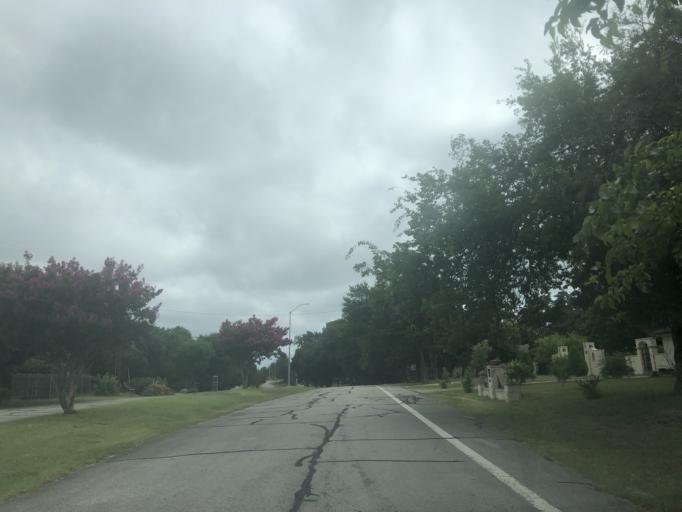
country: US
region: Texas
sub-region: Dallas County
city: Duncanville
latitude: 32.6721
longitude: -96.9150
